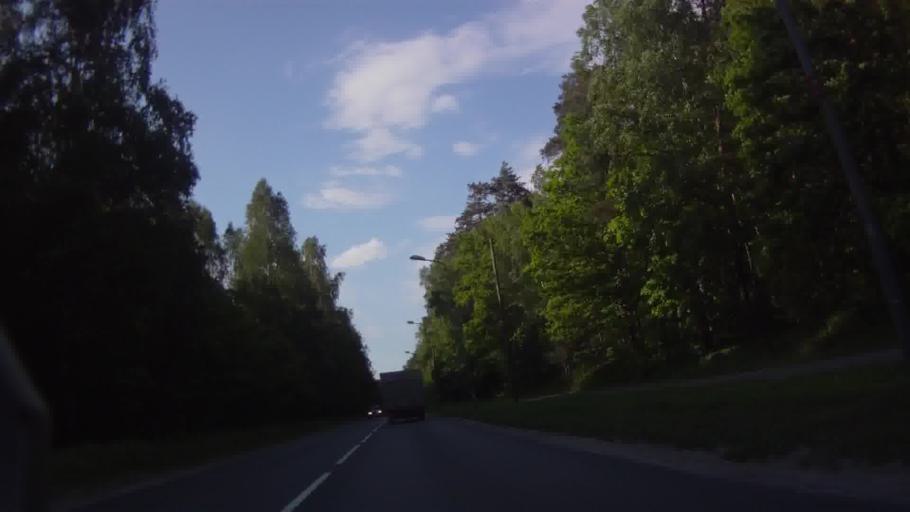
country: LV
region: Stopini
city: Ulbroka
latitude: 56.9625
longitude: 24.2528
